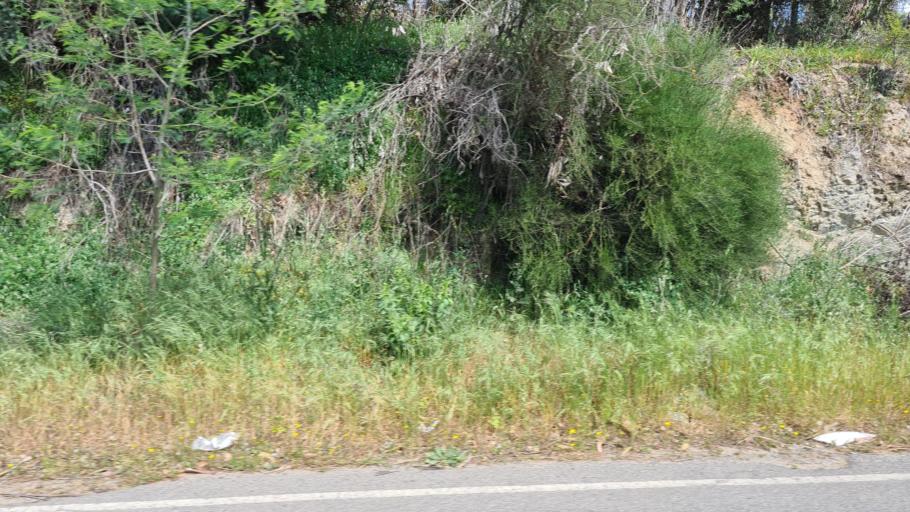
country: CL
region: O'Higgins
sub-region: Provincia de Cachapoal
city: San Vicente
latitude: -34.1560
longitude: -71.4197
